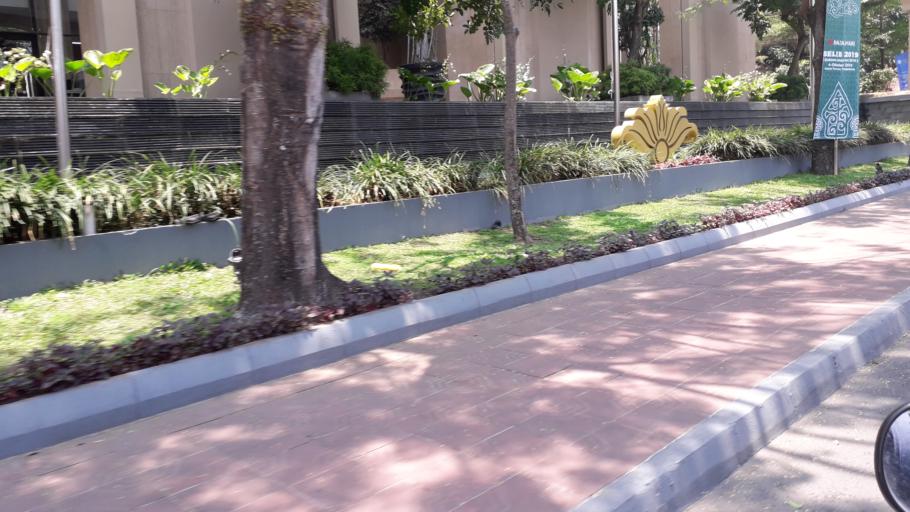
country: ID
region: Daerah Istimewa Yogyakarta
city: Yogyakarta
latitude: -7.7735
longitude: 110.3681
